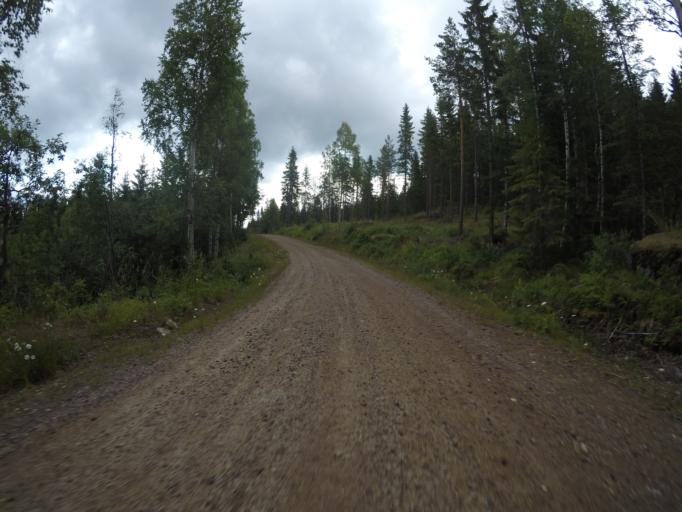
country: SE
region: Vaermland
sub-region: Filipstads Kommun
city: Lesjofors
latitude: 60.1980
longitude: 14.3623
